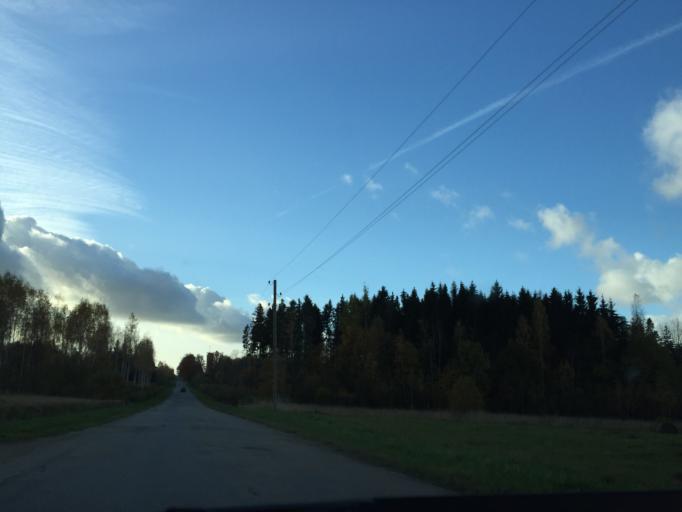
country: LV
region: Ogre
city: Jumprava
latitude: 56.7668
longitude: 25.0140
